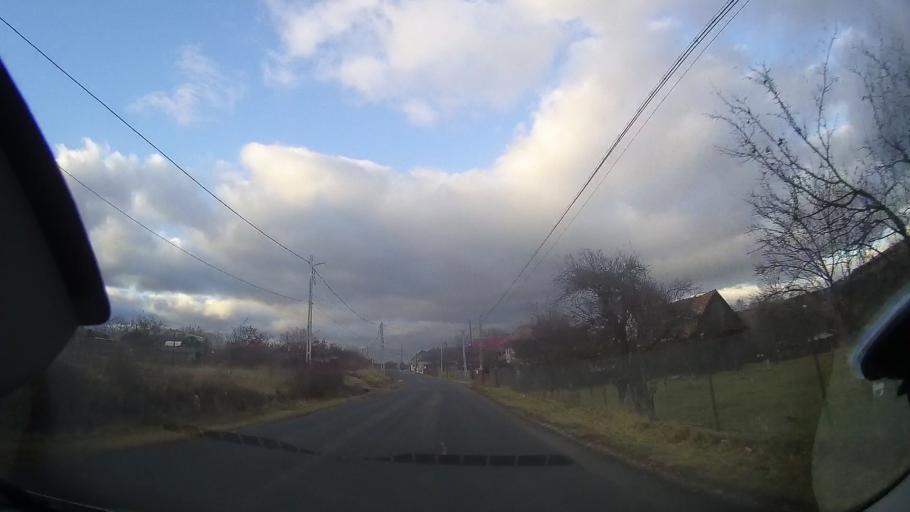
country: RO
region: Cluj
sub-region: Comuna Calatele
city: Calatele
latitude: 46.7731
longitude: 23.0076
